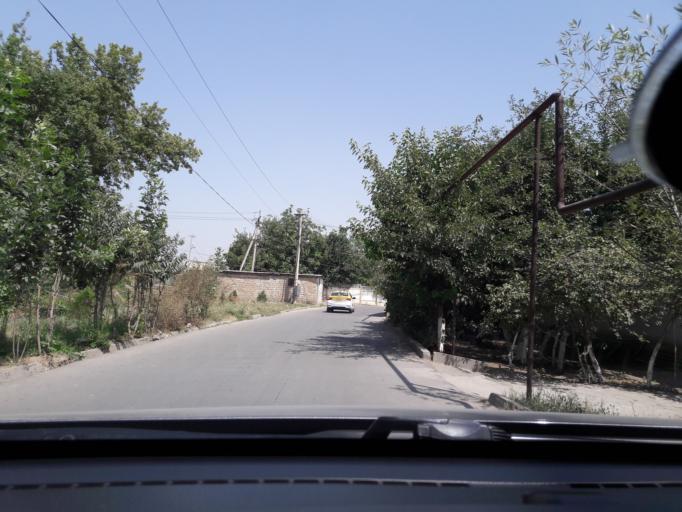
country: TJ
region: Dushanbe
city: Dushanbe
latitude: 38.5866
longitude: 68.7354
